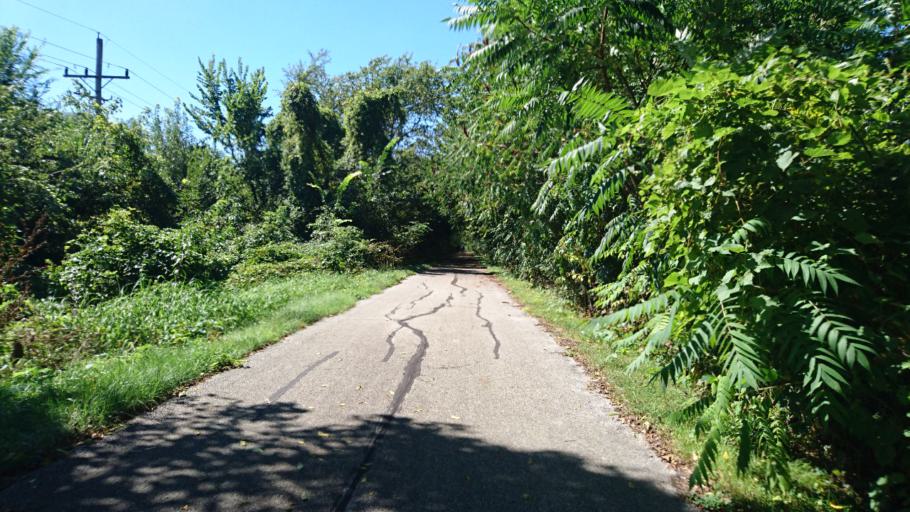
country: US
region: Illinois
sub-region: Cook County
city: Park Forest
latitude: 41.4991
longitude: -87.6766
